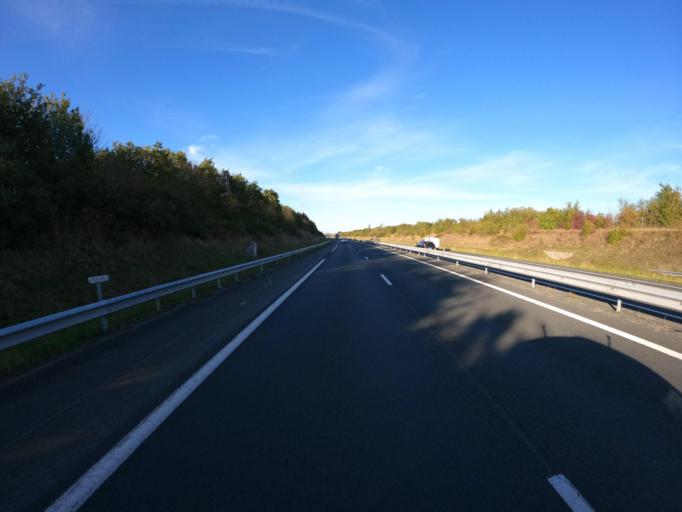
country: FR
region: Pays de la Loire
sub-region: Departement de Maine-et-Loire
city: Mazieres-en-Mauges
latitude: 47.0449
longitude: -0.8399
